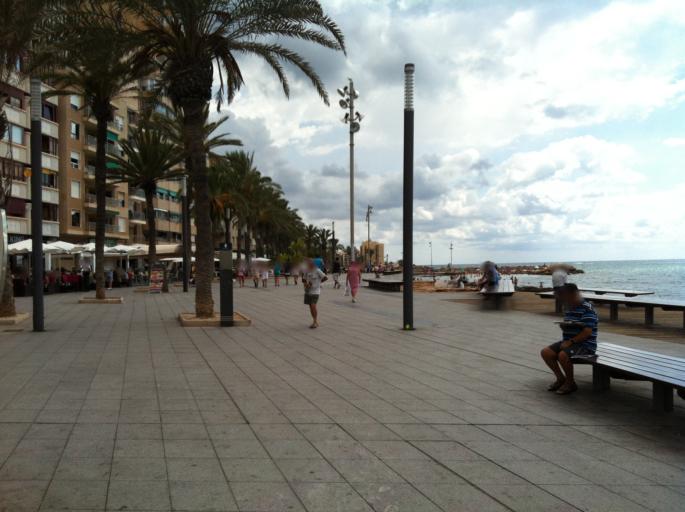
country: ES
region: Valencia
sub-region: Provincia de Alicante
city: Torrevieja
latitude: 37.9741
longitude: -0.6778
